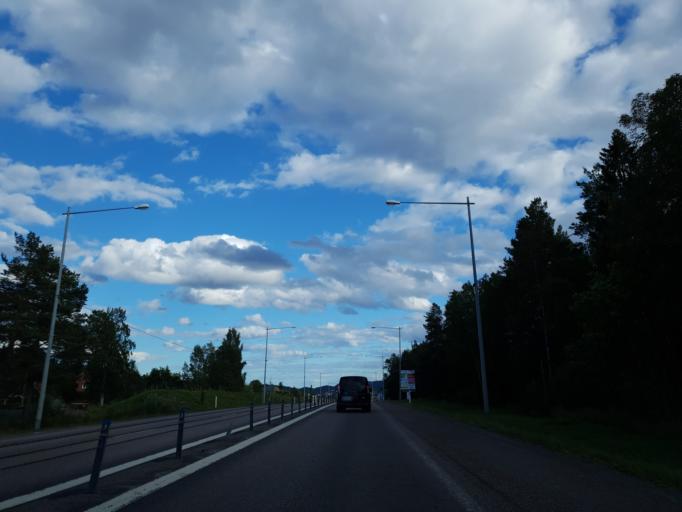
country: SE
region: Vaesternorrland
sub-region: Haernoesands Kommun
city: Haernoesand
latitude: 62.6481
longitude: 17.8977
